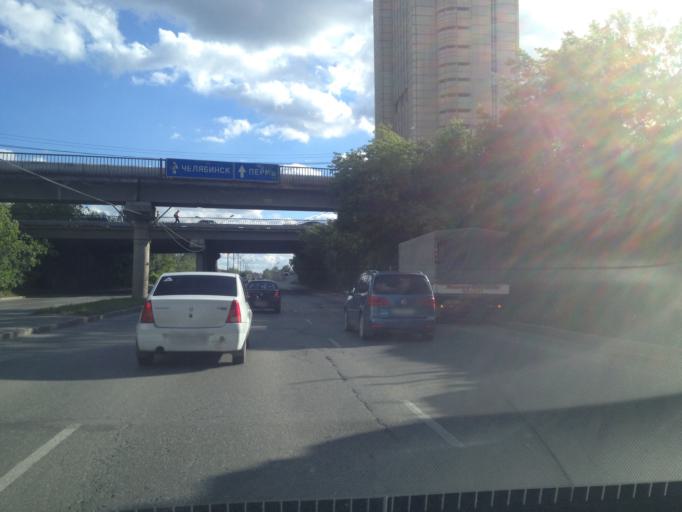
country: RU
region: Sverdlovsk
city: Sovkhoznyy
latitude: 56.8149
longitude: 60.5522
